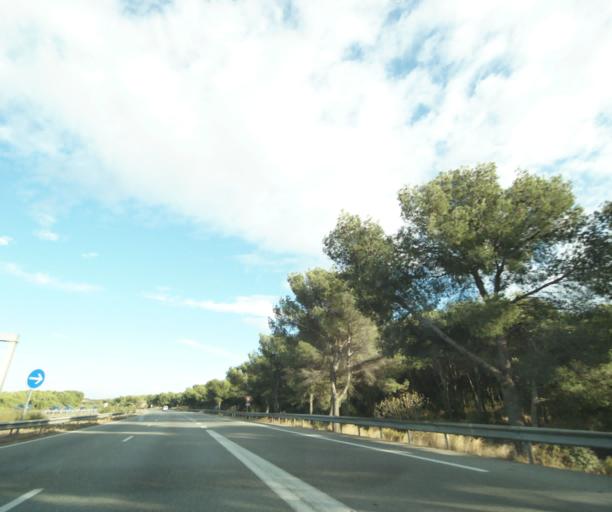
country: FR
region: Provence-Alpes-Cote d'Azur
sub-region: Departement des Bouches-du-Rhone
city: Ensues-la-Redonne
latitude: 43.3730
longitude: 5.1903
